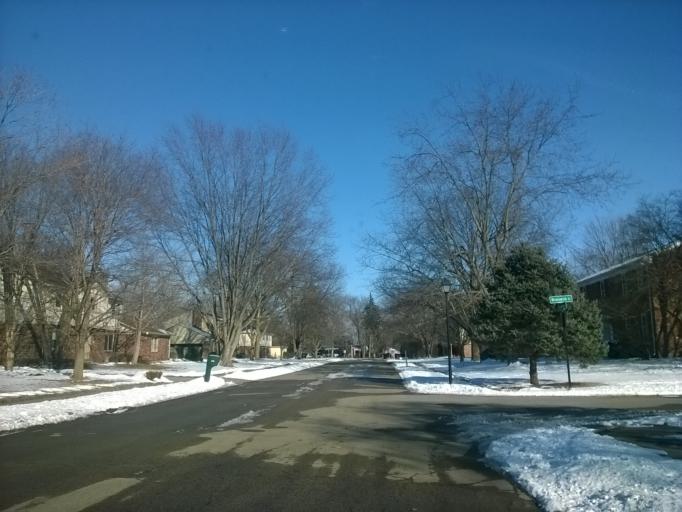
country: US
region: Indiana
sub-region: Hamilton County
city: Carmel
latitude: 39.9482
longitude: -86.1001
